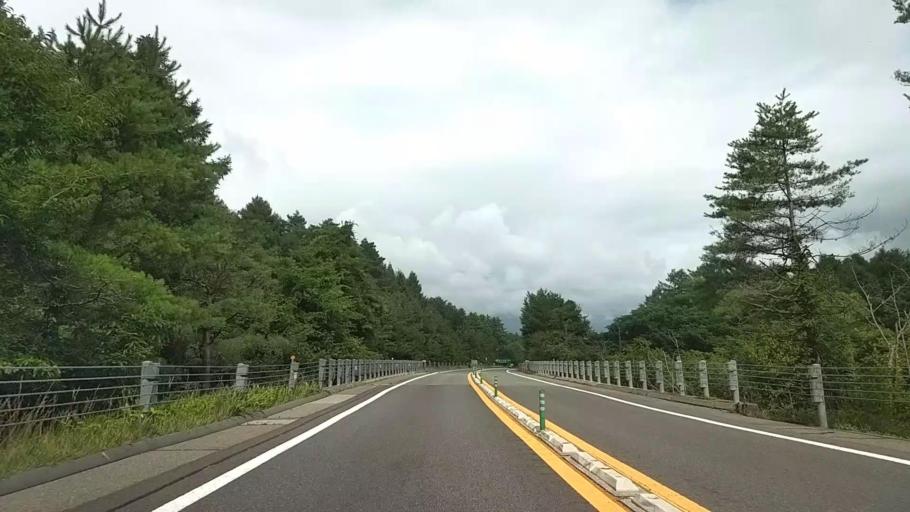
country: JP
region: Yamanashi
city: Fujikawaguchiko
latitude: 35.4591
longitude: 138.7802
